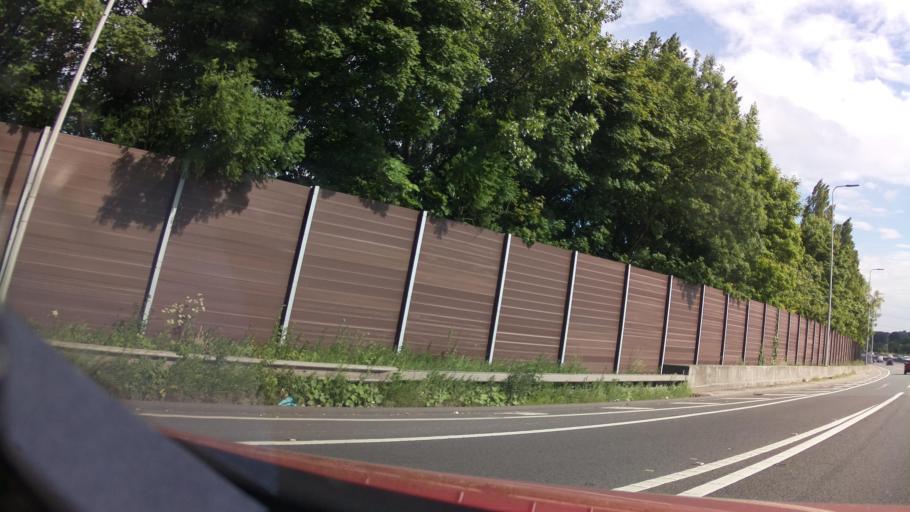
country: GB
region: England
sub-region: City and Borough of Salford
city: Walkden
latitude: 53.4982
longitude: -2.3846
